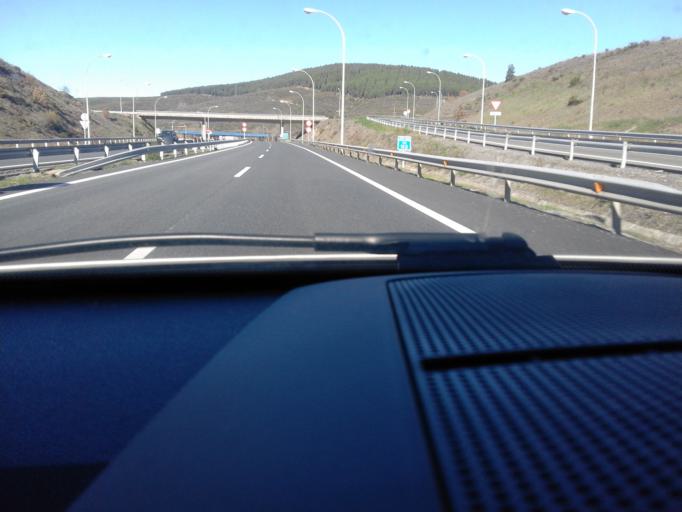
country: ES
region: Castille and Leon
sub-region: Provincia de Leon
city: Carrocera
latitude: 42.7802
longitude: -5.7846
